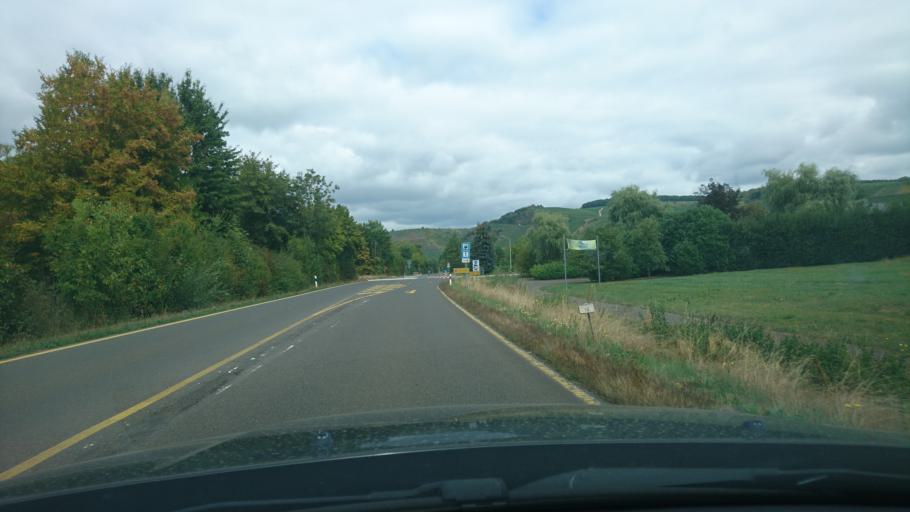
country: DE
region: Rheinland-Pfalz
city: Wiltingen
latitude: 49.6611
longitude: 6.5872
